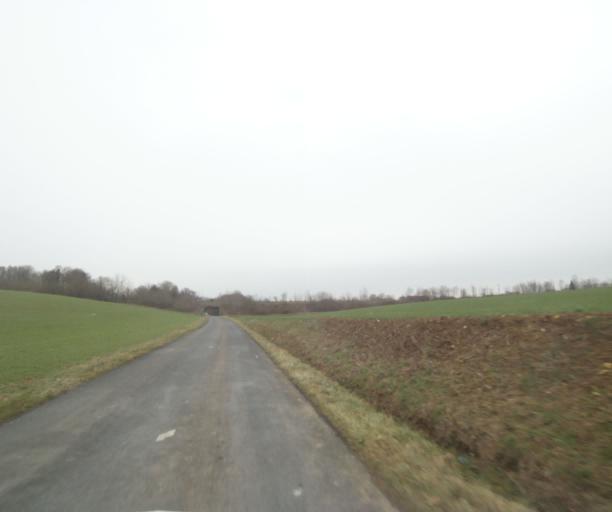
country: FR
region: Champagne-Ardenne
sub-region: Departement de la Haute-Marne
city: Bienville
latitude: 48.5772
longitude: 5.0304
